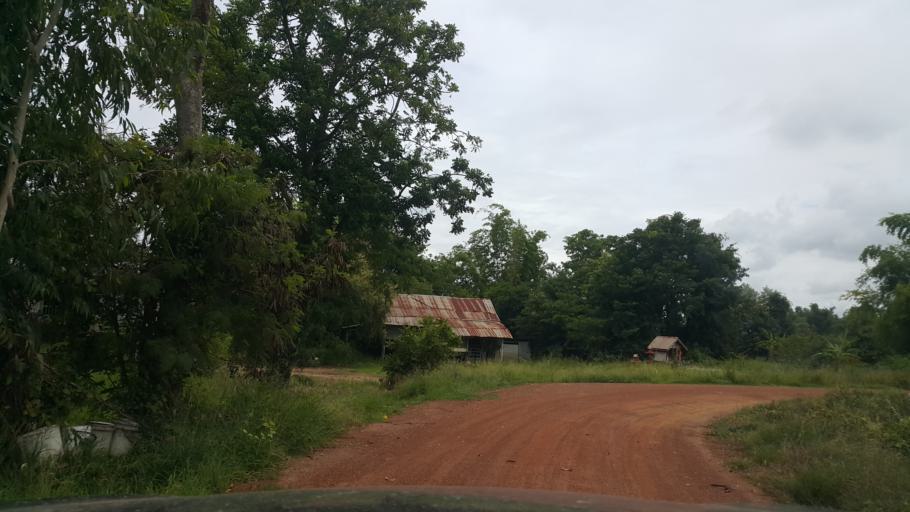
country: TH
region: Phitsanulok
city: Bang Rakam
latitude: 16.8438
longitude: 100.0649
